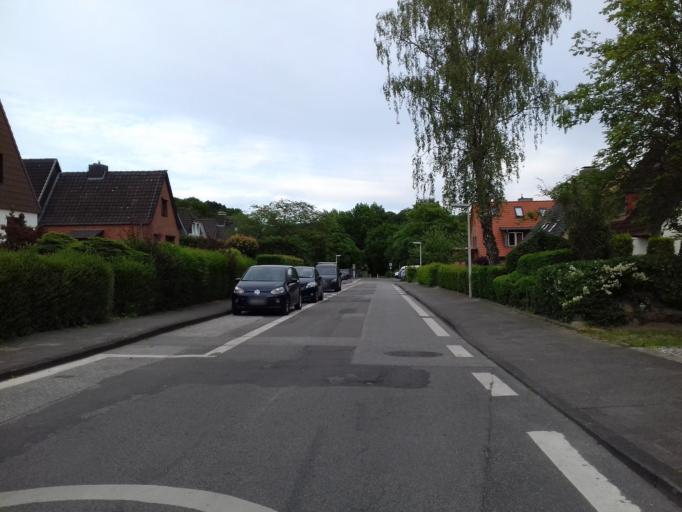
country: DE
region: Schleswig-Holstein
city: Kronshagen
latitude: 54.3191
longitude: 10.0691
